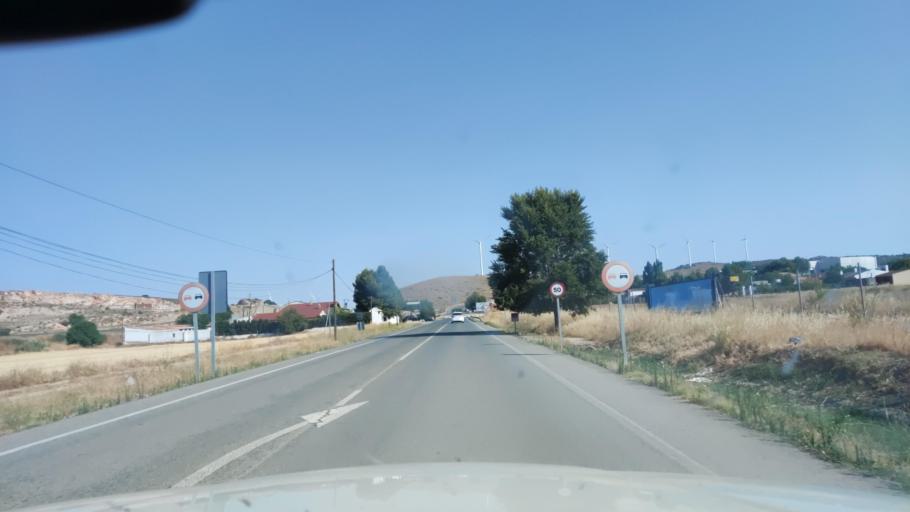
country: ES
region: Castille-La Mancha
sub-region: Provincia de Albacete
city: Pozo-Canada
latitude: 38.7975
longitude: -1.7281
